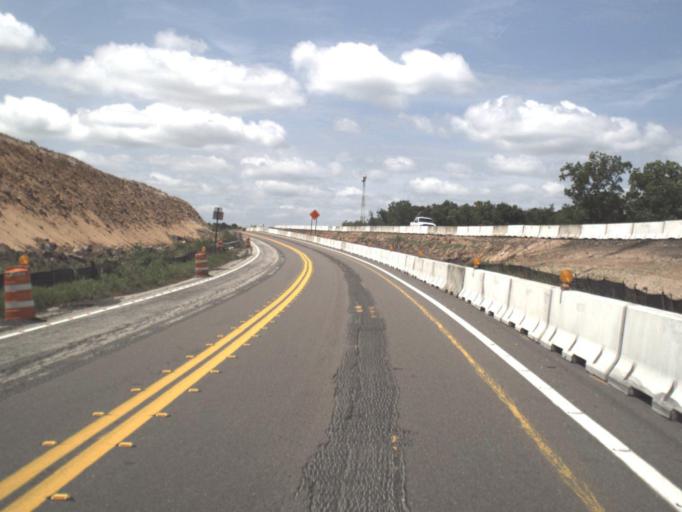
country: US
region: Florida
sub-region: Nassau County
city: Nassau Village-Ratliff
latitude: 30.5103
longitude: -81.8768
